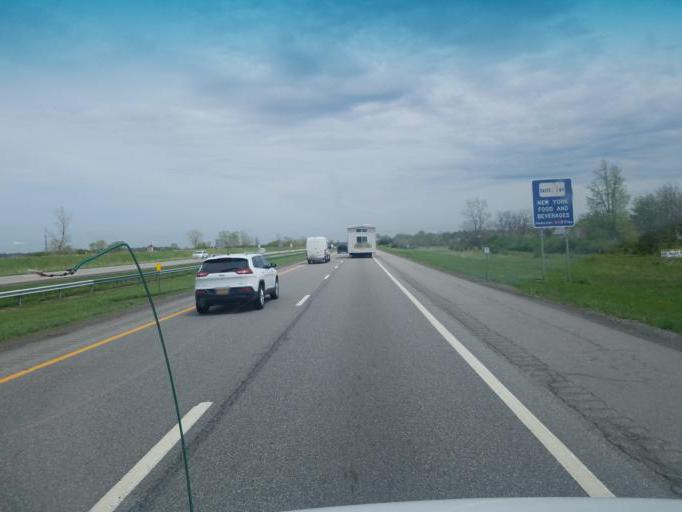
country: US
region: New York
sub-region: Erie County
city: Harris Hill
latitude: 42.9471
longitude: -78.6692
